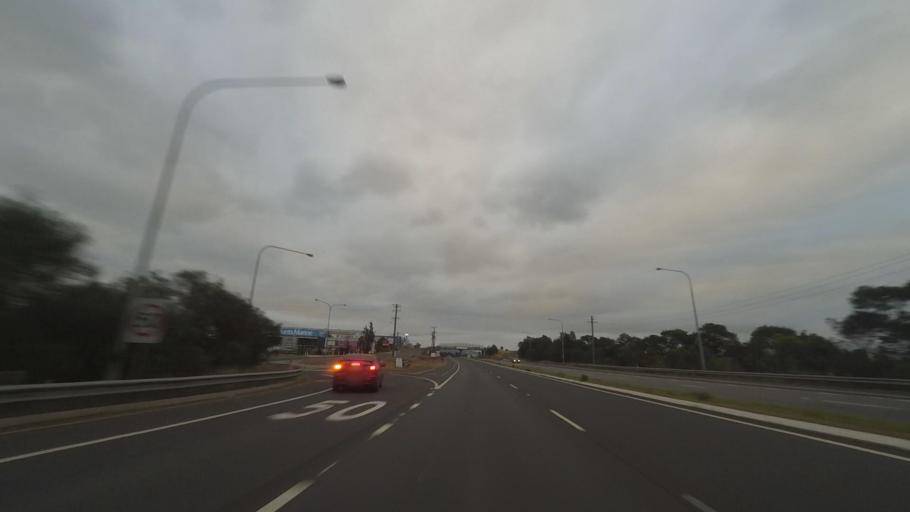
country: AU
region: New South Wales
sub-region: Shellharbour
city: Albion Park Rail
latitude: -34.5446
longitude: 150.7850
